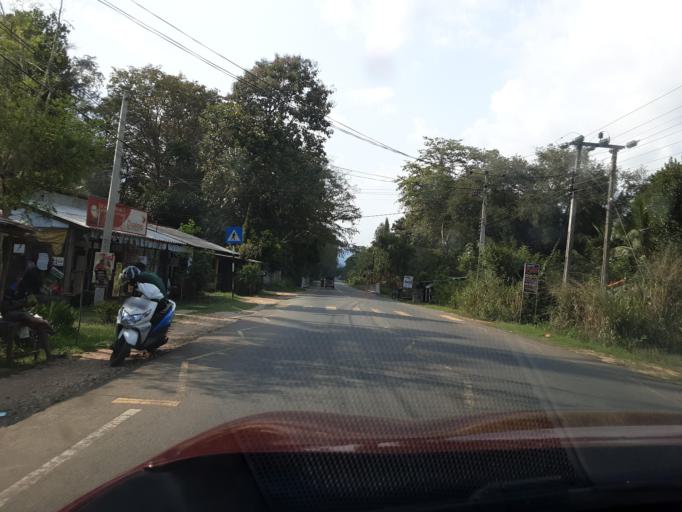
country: LK
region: Uva
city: Haputale
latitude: 6.6796
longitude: 81.1105
